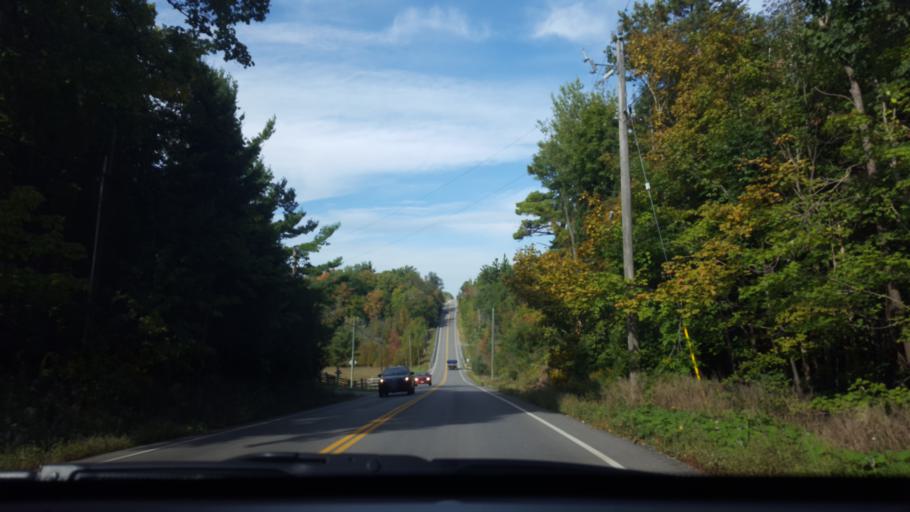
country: CA
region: Ontario
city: Vaughan
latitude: 43.8437
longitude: -79.5872
